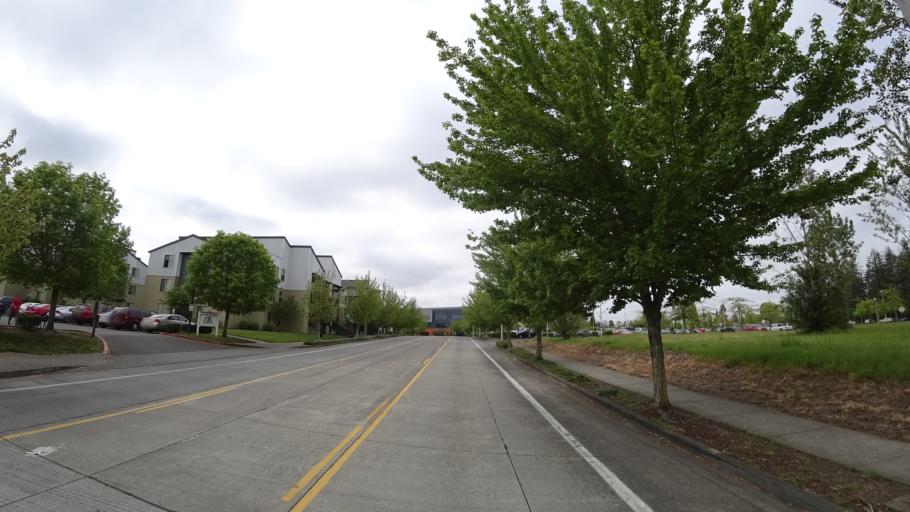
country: US
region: Oregon
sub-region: Washington County
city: Aloha
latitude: 45.5197
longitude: -122.8704
